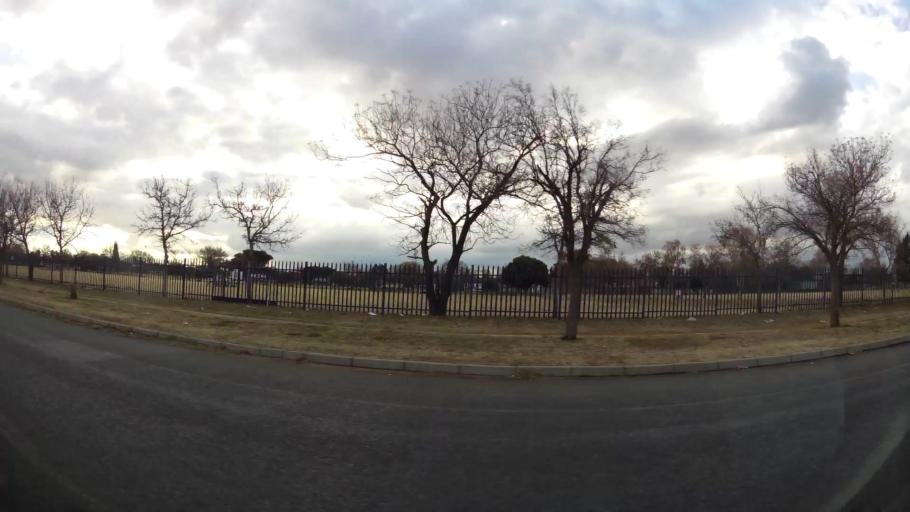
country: ZA
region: Orange Free State
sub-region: Lejweleputswa District Municipality
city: Welkom
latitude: -27.9807
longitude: 26.7306
